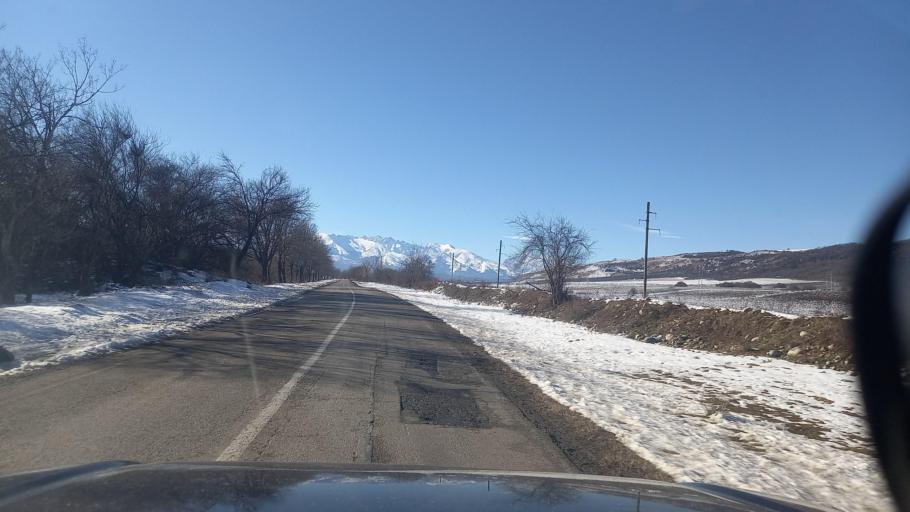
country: RU
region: North Ossetia
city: Chikola
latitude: 43.2436
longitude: 43.9563
